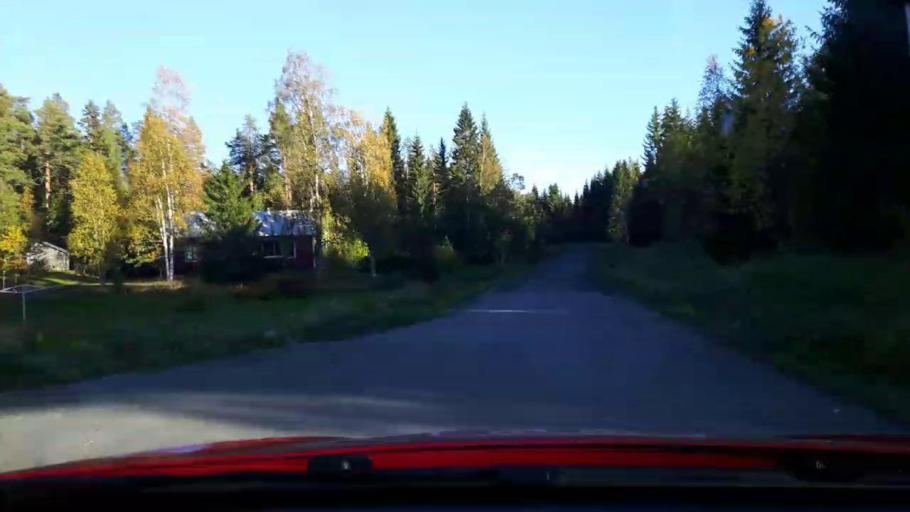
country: SE
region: Jaemtland
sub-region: OEstersunds Kommun
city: Lit
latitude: 63.6086
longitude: 14.7805
